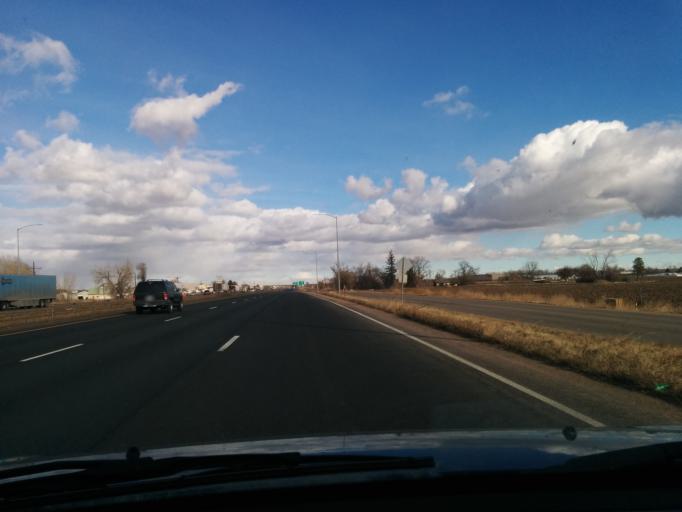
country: US
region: Colorado
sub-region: Larimer County
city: Fort Collins
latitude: 40.5703
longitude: -105.0012
